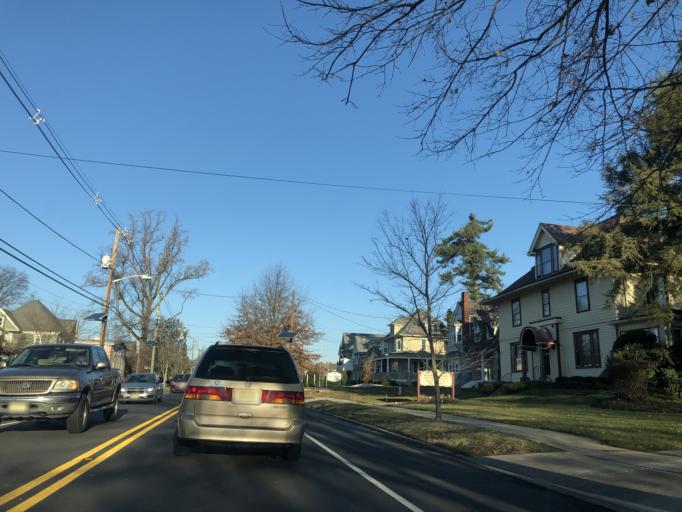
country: US
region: New Jersey
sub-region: Camden County
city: Haddon Heights
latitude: 39.8844
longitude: -75.0582
